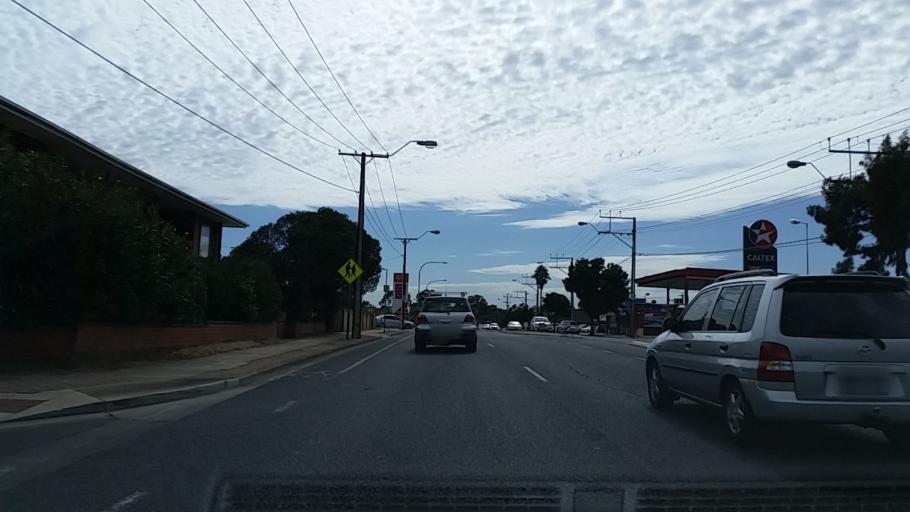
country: AU
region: South Australia
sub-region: Campbelltown
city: Hectorville
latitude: -34.8862
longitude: 138.6585
